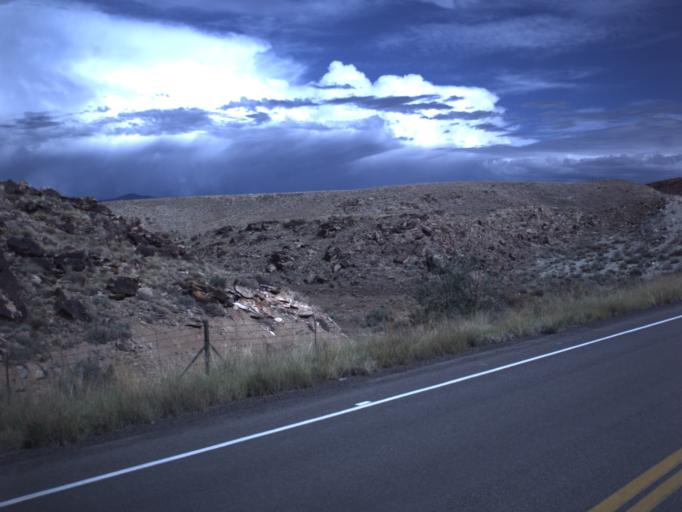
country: US
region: Colorado
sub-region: Montezuma County
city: Towaoc
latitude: 37.1730
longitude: -109.0991
